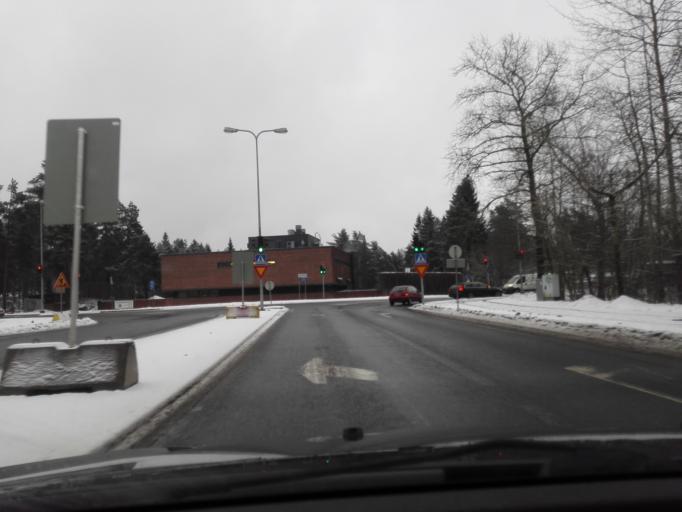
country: FI
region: Uusimaa
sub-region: Helsinki
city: Vantaa
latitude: 60.2874
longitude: 25.0800
